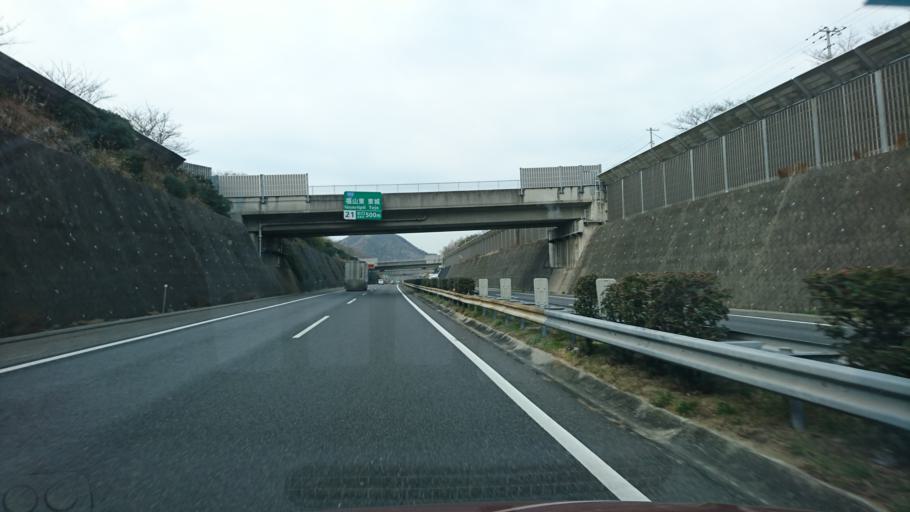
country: JP
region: Hiroshima
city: Kannabecho-yahiro
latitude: 34.5129
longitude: 133.4054
